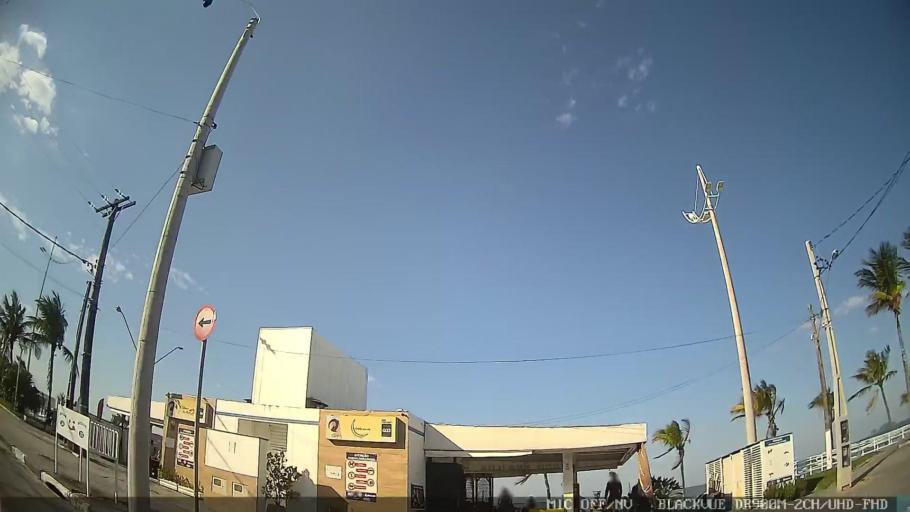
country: BR
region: Sao Paulo
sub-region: Guaruja
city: Guaruja
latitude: -23.9855
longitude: -46.2219
